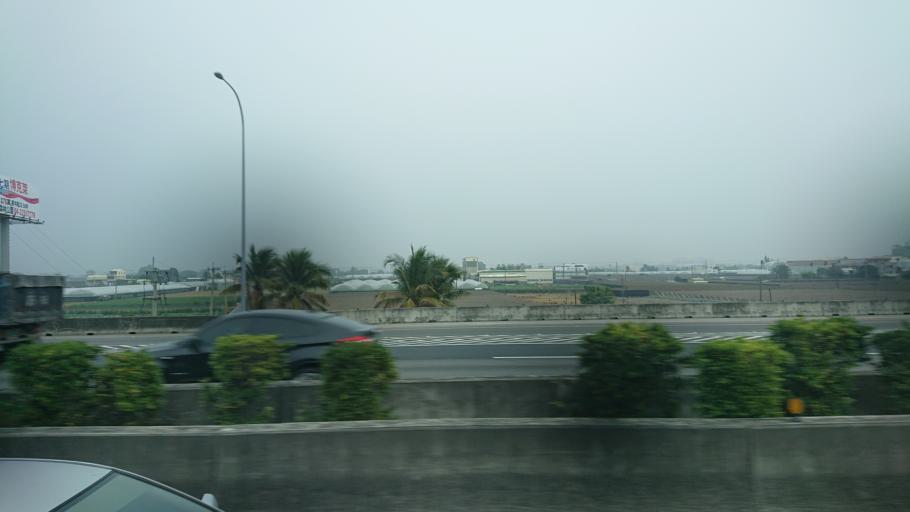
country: TW
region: Taiwan
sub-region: Changhua
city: Chang-hua
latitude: 23.9580
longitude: 120.5065
